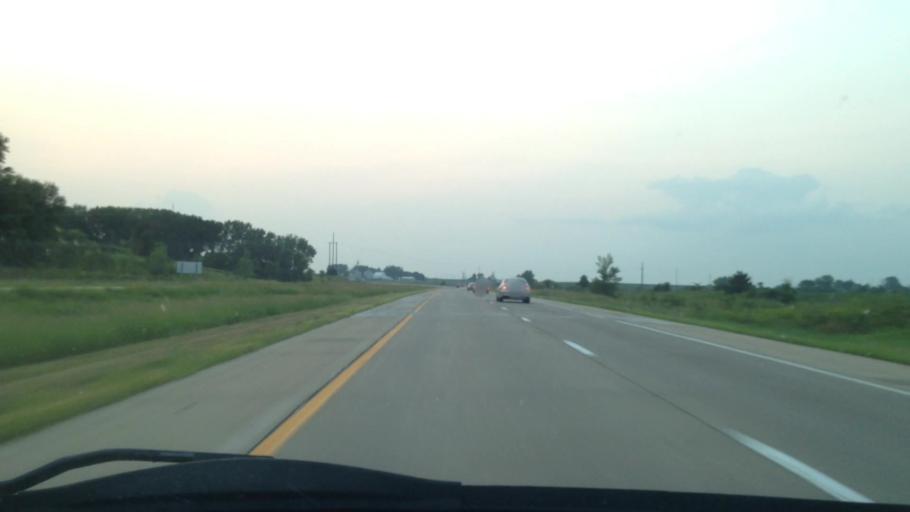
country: US
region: Iowa
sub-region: Benton County
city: Urbana
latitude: 42.3235
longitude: -91.9914
